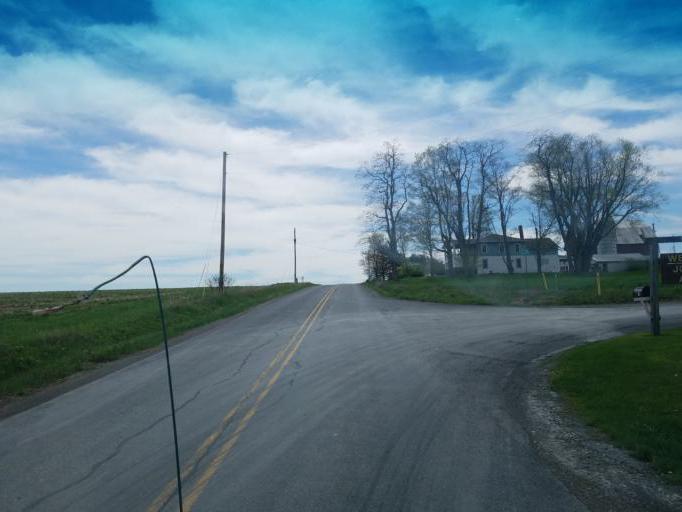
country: US
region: Pennsylvania
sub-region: Tioga County
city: Wellsboro
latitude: 41.7268
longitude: -77.3876
